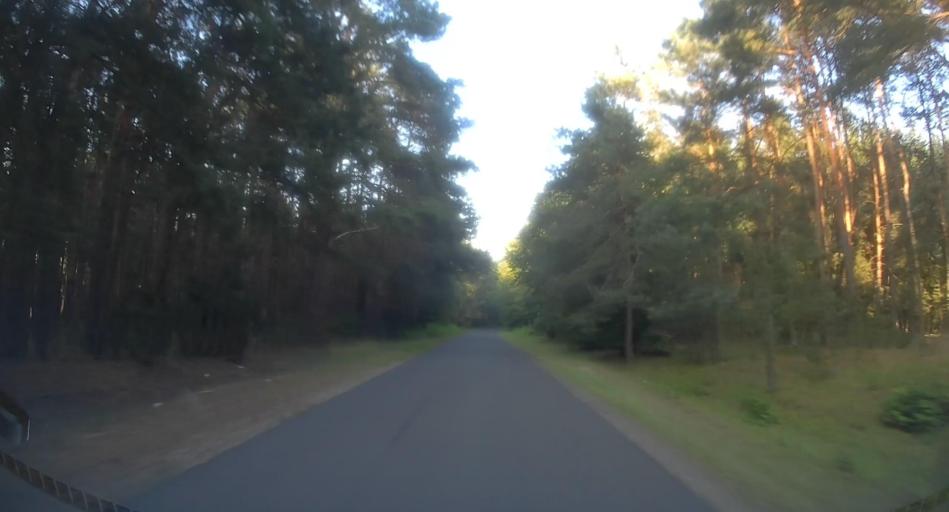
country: PL
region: Masovian Voivodeship
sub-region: Powiat zyrardowski
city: Puszcza Marianska
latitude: 51.9065
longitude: 20.3321
